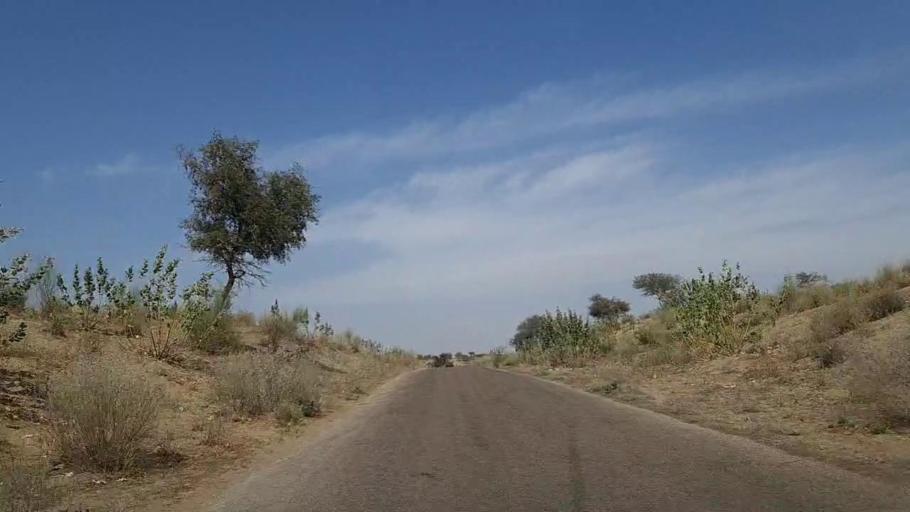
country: PK
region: Sindh
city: Umarkot
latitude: 25.1321
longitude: 70.0085
